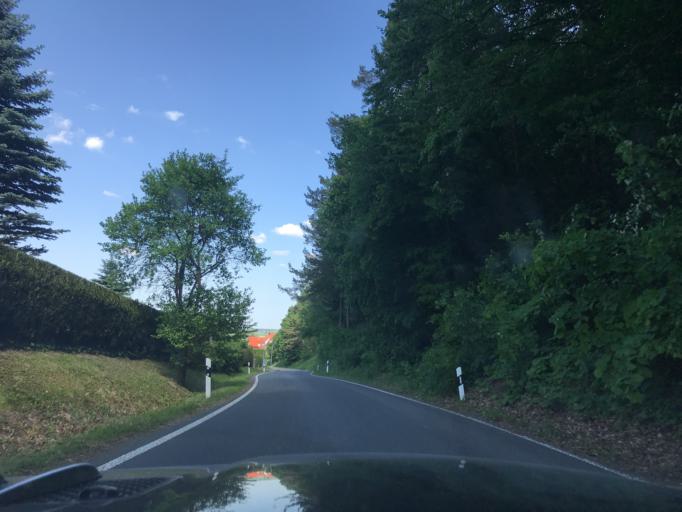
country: DE
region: Thuringia
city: Behringen
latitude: 50.7841
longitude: 10.9870
